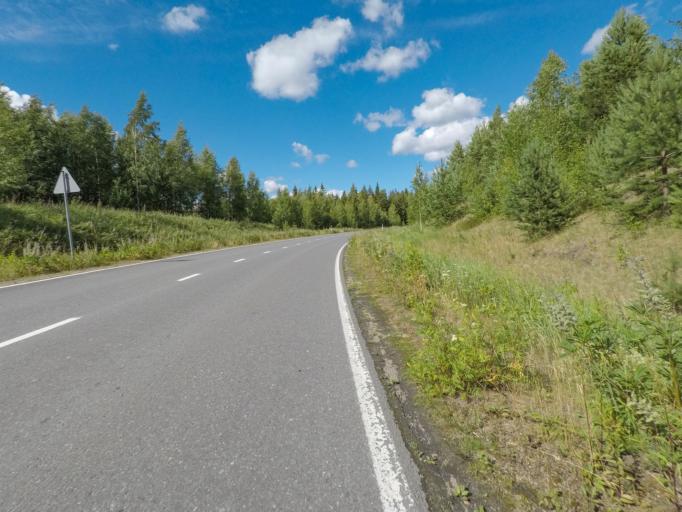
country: FI
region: South Karelia
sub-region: Lappeenranta
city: Joutseno
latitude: 61.0928
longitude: 28.3524
